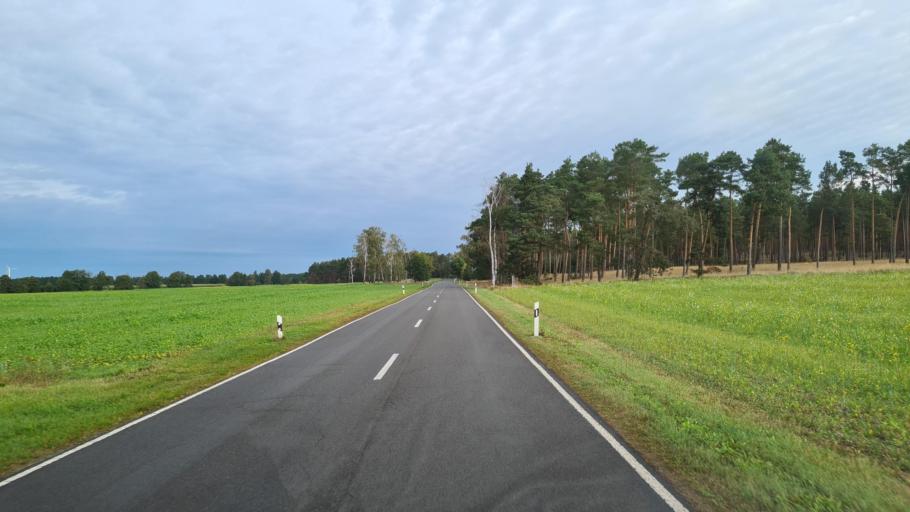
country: DE
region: Brandenburg
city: Kasel-Golzig
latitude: 51.9050
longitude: 13.7143
